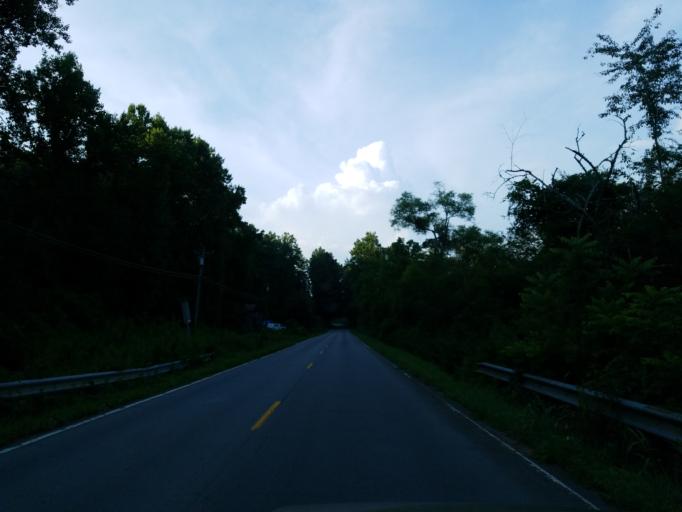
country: US
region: Georgia
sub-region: Gilmer County
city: Ellijay
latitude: 34.5984
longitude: -84.5286
